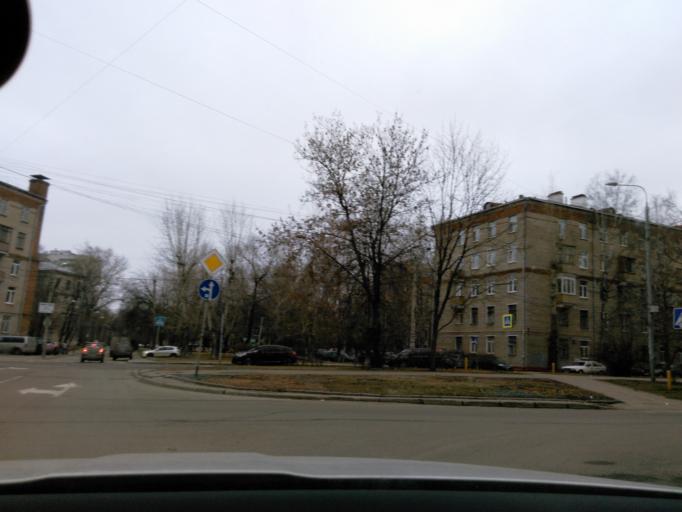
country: RU
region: Moskovskaya
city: Koptevo
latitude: 55.8279
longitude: 37.5245
